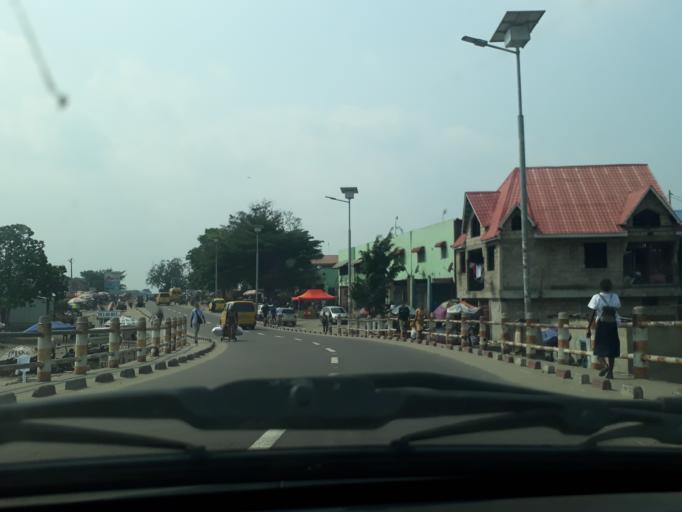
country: CD
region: Kinshasa
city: Kinshasa
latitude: -4.3324
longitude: 15.3215
